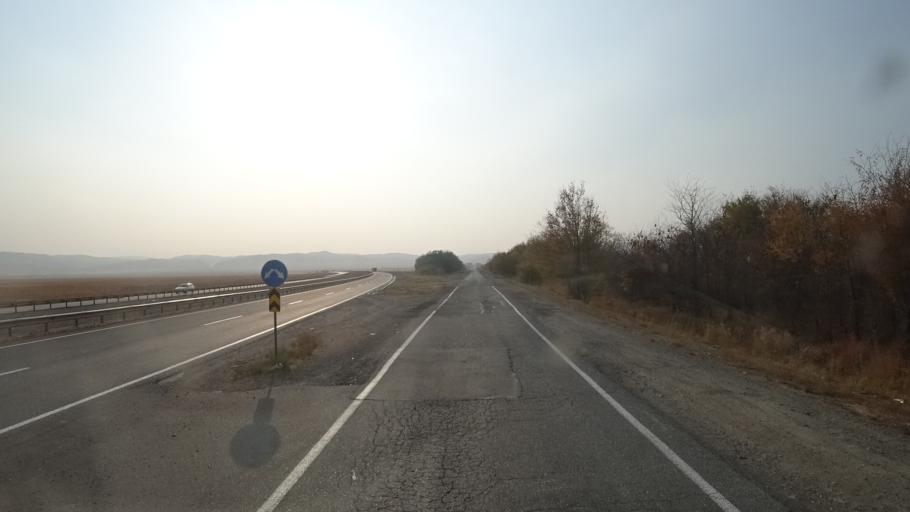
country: KZ
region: Zhambyl
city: Taraz
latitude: 42.7858
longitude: 71.0524
